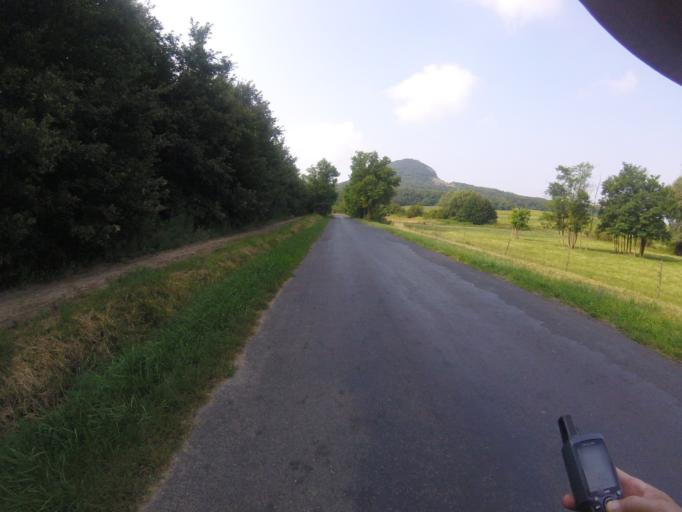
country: HU
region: Veszprem
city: Badacsonytomaj
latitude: 46.8389
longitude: 17.5116
